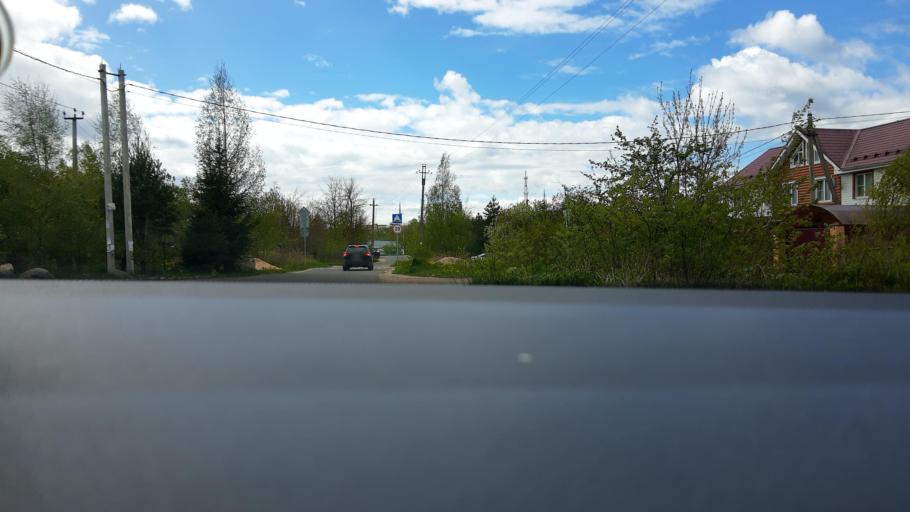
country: RU
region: Moskovskaya
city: Dmitrov
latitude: 56.3547
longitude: 37.5443
